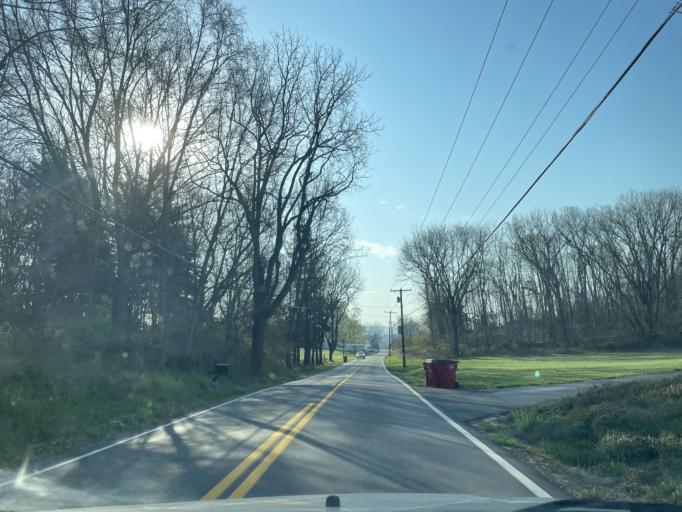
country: US
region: Maryland
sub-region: Washington County
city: Saint James
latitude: 39.5465
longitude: -77.7229
